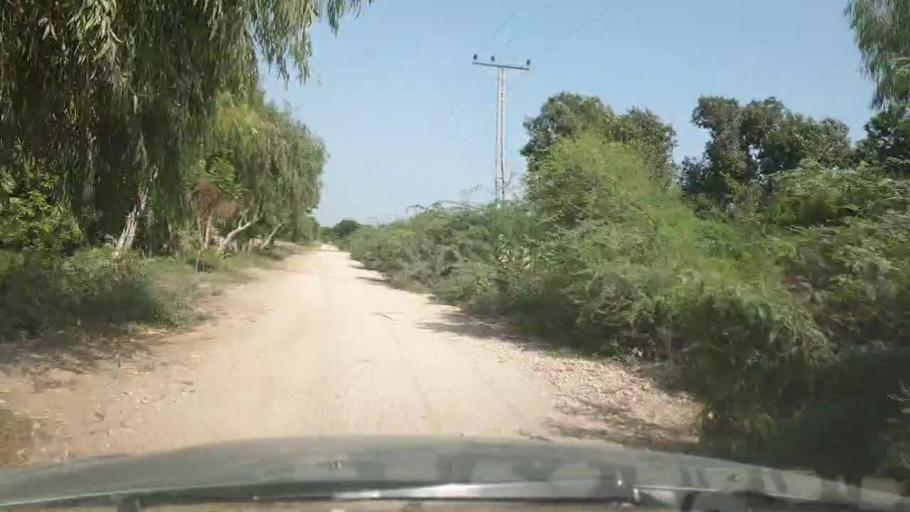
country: PK
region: Sindh
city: Tando Ghulam Ali
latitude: 25.1937
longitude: 68.8851
